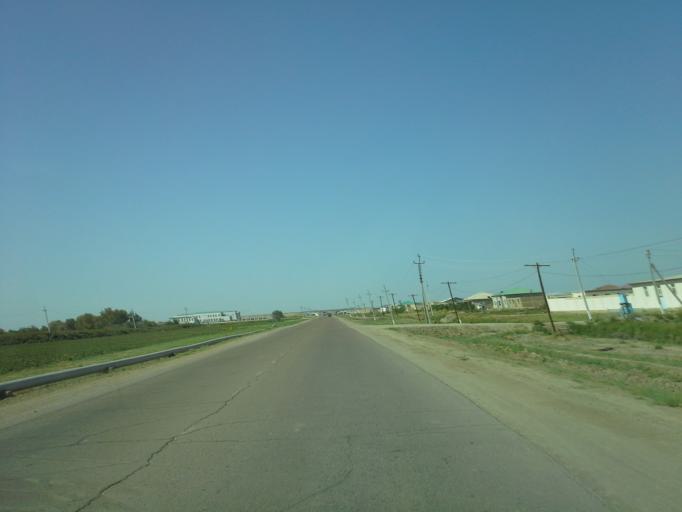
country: TM
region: Dasoguz
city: Dasoguz
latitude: 41.7921
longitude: 60.0217
